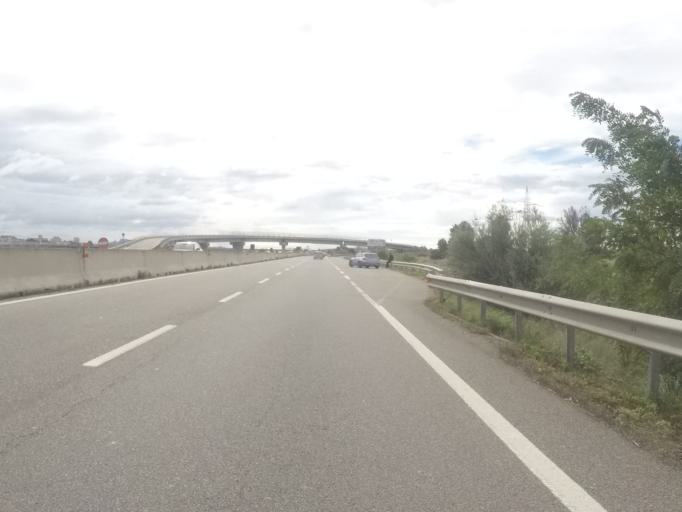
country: IT
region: Sardinia
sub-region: Provincia di Cagliari
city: Cagliari
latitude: 39.2219
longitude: 9.0823
